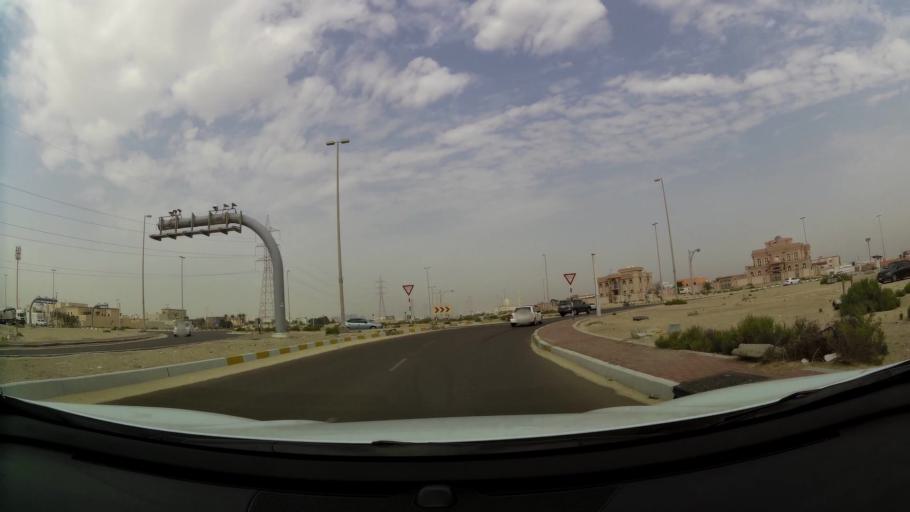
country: AE
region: Abu Dhabi
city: Abu Dhabi
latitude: 24.3103
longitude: 54.6436
